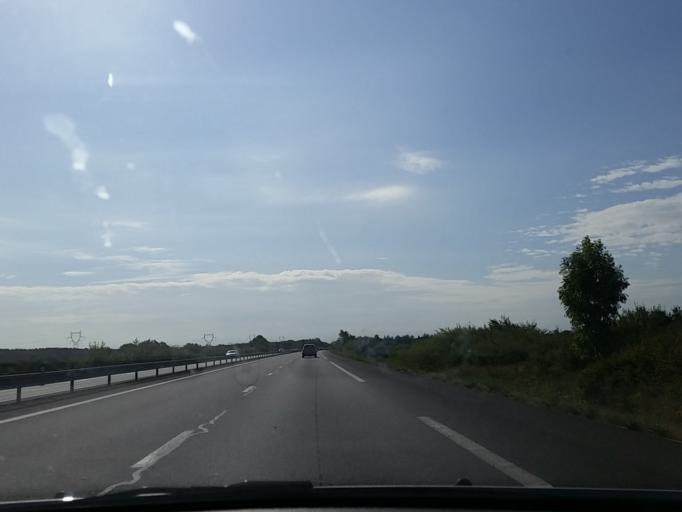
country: FR
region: Centre
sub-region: Departement du Cher
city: Marmagne
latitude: 47.0862
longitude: 2.2600
